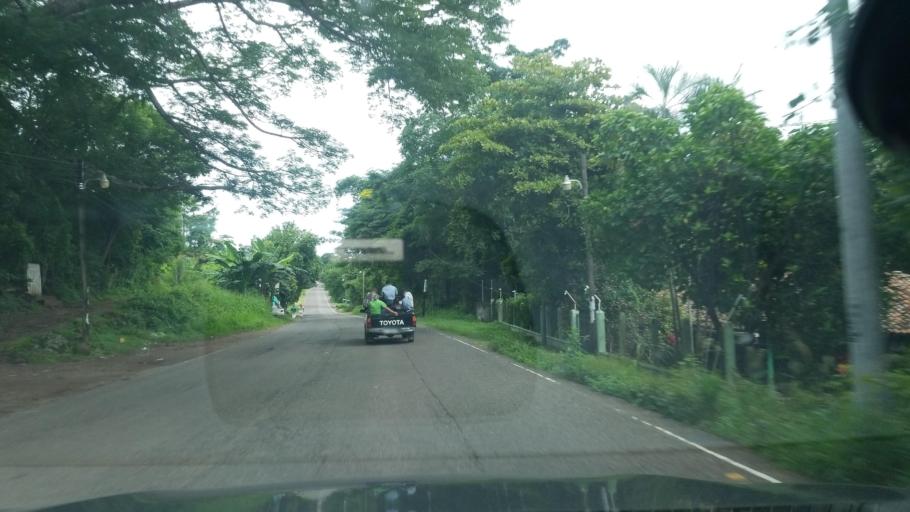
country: HN
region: Choluteca
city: Corpus
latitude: 13.3692
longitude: -87.0279
